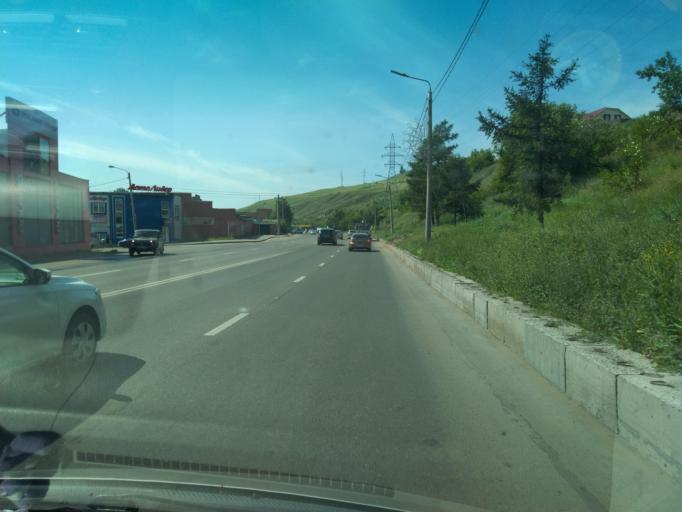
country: RU
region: Krasnoyarskiy
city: Krasnoyarsk
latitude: 56.0203
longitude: 92.8742
